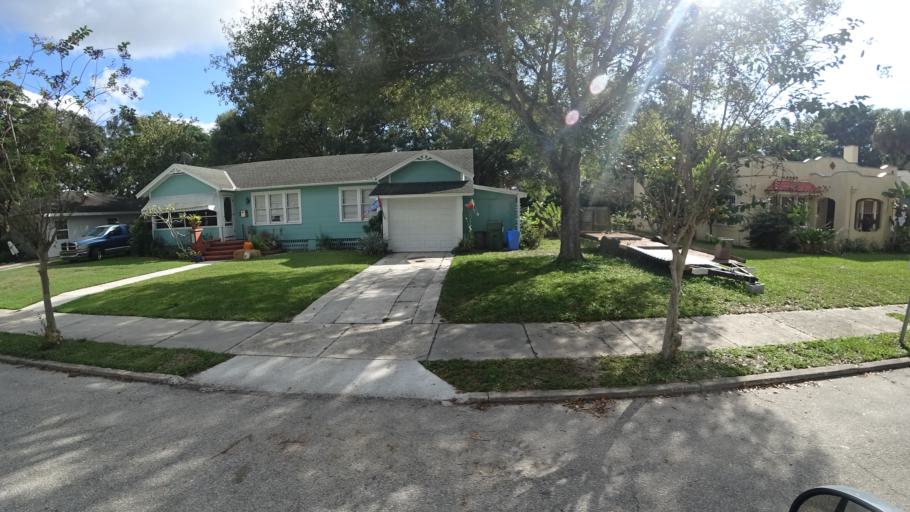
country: US
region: Florida
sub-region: Manatee County
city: Bradenton
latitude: 27.4946
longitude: -82.5856
